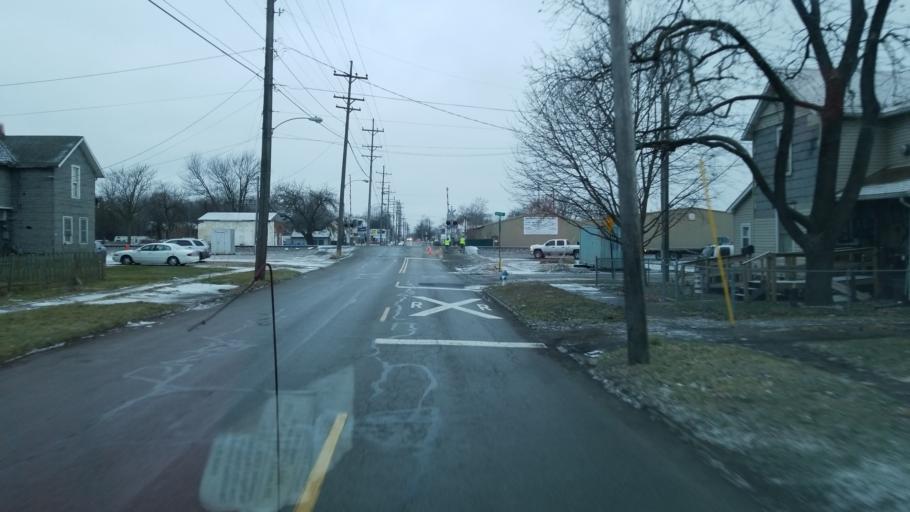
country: US
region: Ohio
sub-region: Marion County
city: Marion
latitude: 40.5931
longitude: -83.1396
